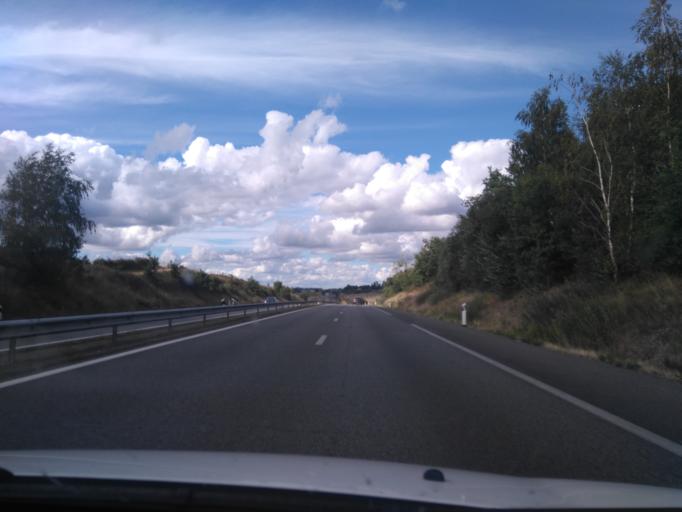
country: FR
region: Brittany
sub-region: Departement d'Ille-et-Vilaine
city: Pance
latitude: 47.8766
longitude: -1.6891
